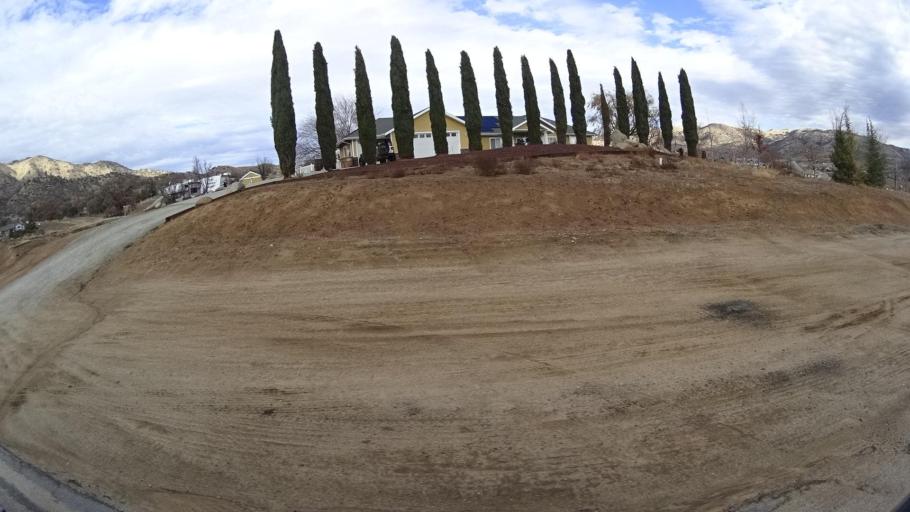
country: US
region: California
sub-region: Kern County
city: Golden Hills
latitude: 35.1538
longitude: -118.4998
